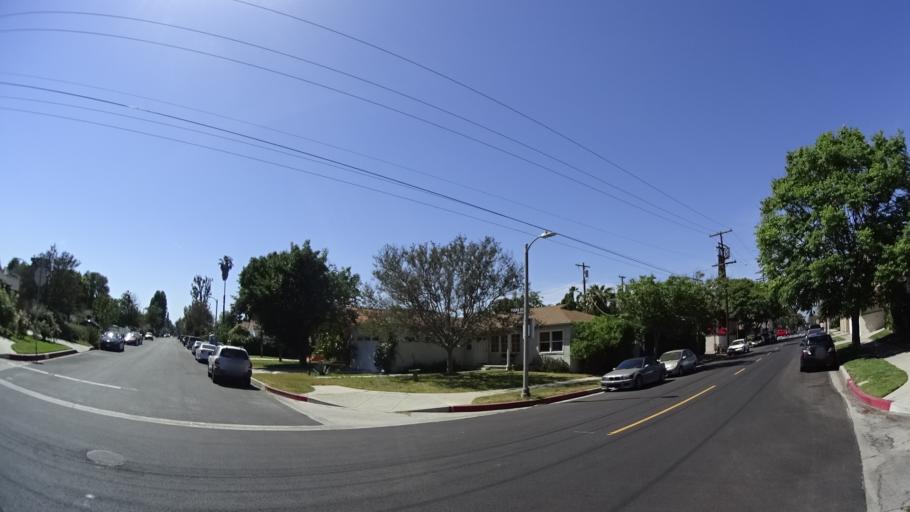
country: US
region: California
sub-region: Los Angeles County
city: North Hollywood
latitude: 34.1785
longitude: -118.4094
